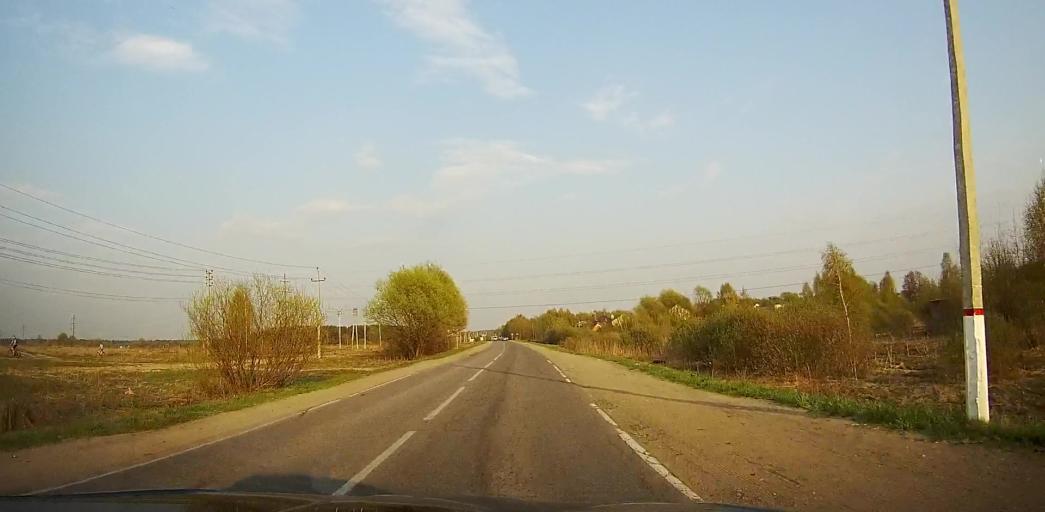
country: RU
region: Moskovskaya
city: Ramenskoye
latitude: 55.5795
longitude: 38.2725
